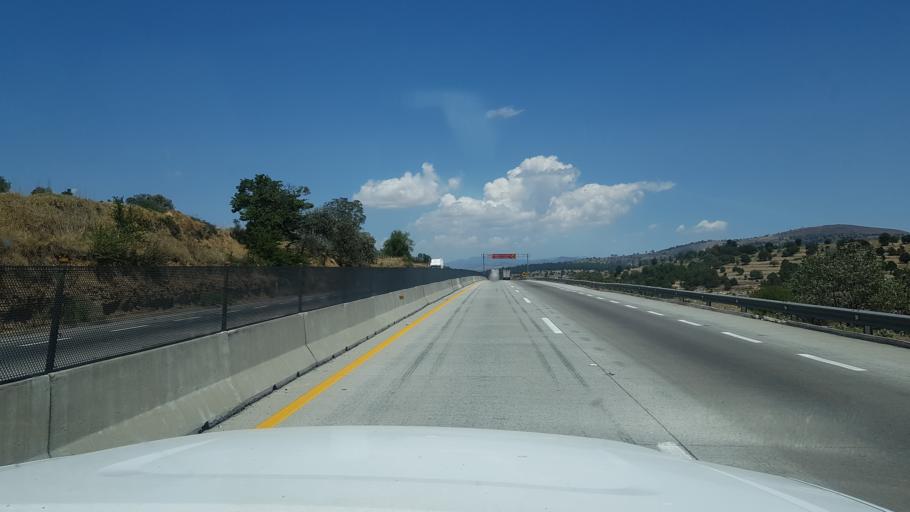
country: MX
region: Tlaxcala
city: Sanctorum
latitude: 19.4941
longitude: -98.4630
